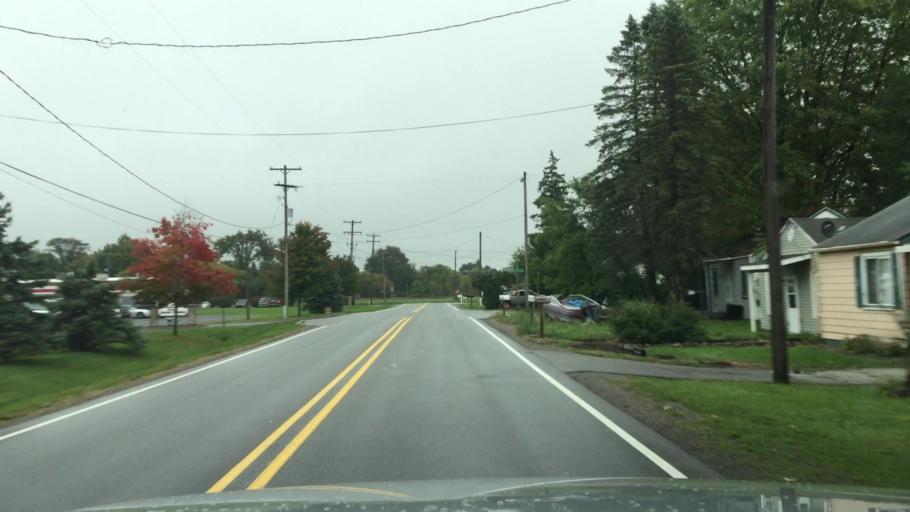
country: US
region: Michigan
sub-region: Saginaw County
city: Buena Vista
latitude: 43.3949
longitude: -83.9113
